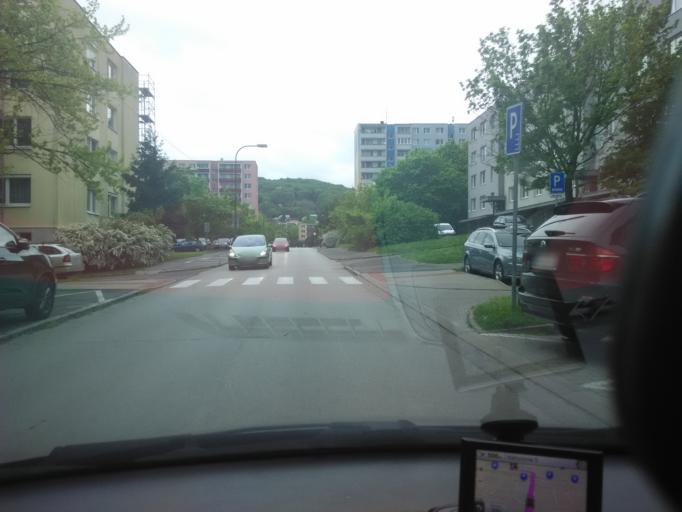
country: AT
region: Lower Austria
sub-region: Politischer Bezirk Bruck an der Leitha
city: Wolfsthal
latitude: 48.1823
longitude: 17.0445
